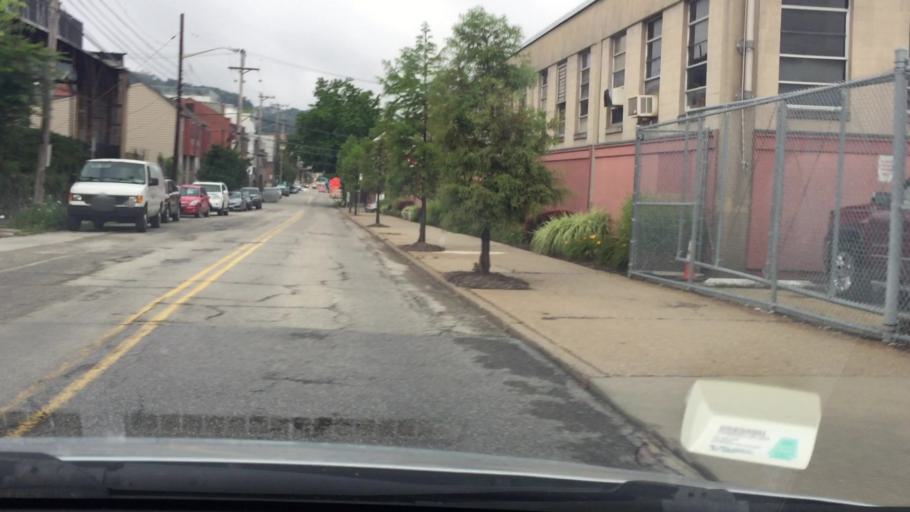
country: US
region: Pennsylvania
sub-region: Allegheny County
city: Pittsburgh
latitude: 40.4301
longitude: -79.9842
